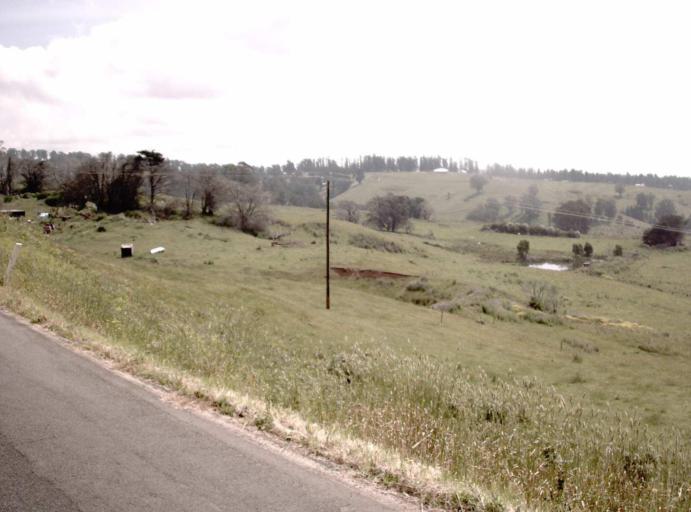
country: AU
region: Victoria
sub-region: Latrobe
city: Traralgon
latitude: -38.3388
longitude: 146.5730
